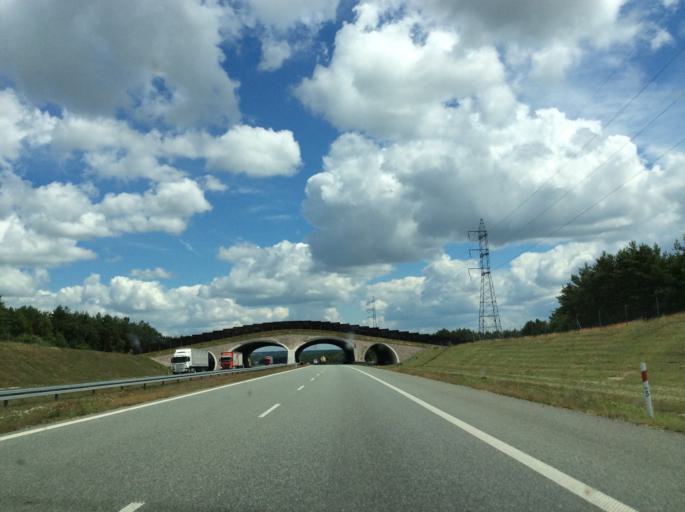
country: PL
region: Greater Poland Voivodeship
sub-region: Powiat turecki
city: Tuliszkow
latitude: 52.1401
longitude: 18.3506
